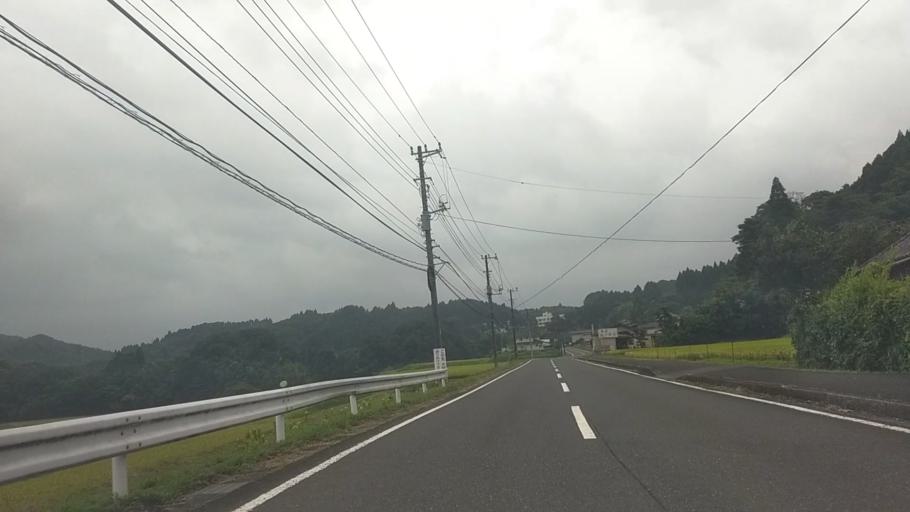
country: JP
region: Chiba
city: Kawaguchi
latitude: 35.2585
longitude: 140.0557
